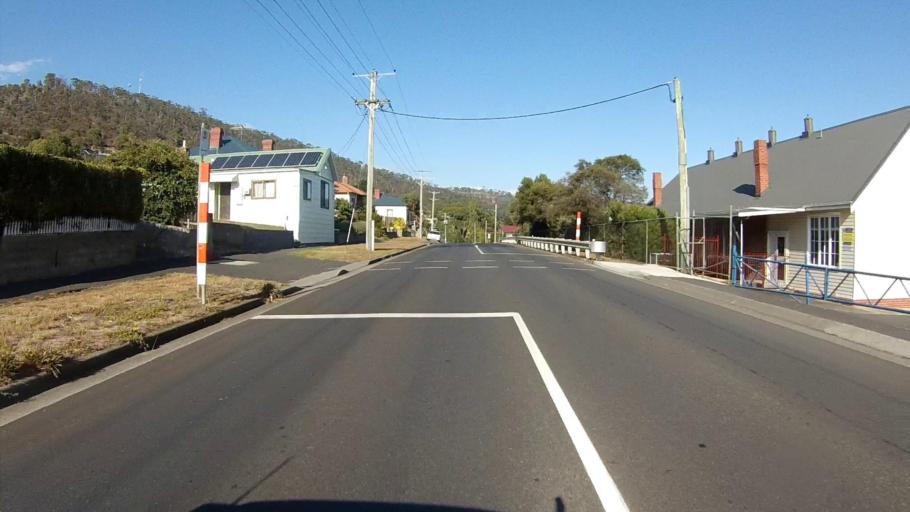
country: AU
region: Tasmania
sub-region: Derwent Valley
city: New Norfolk
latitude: -42.7808
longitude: 147.0562
